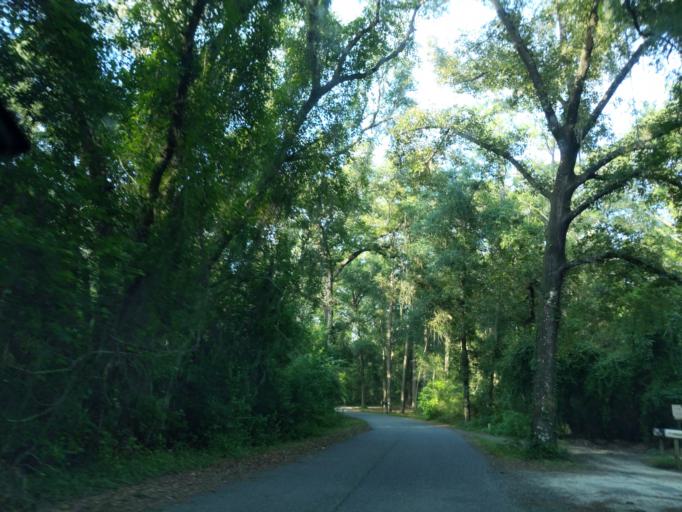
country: US
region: Florida
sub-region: Leon County
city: Woodville
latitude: 30.3492
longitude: -84.3644
